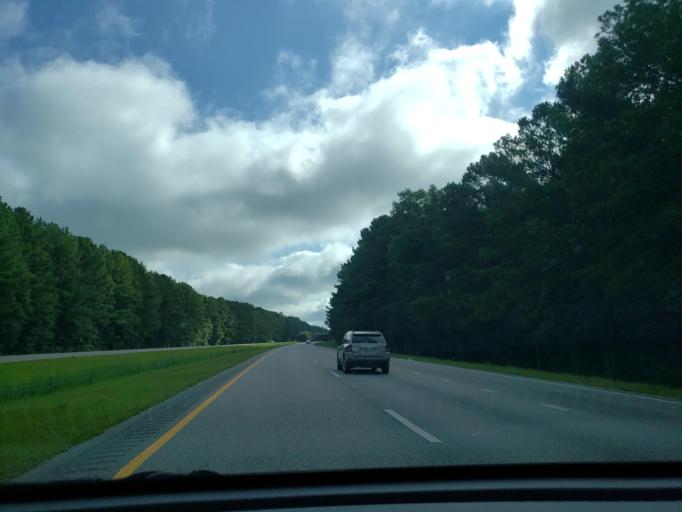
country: US
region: North Carolina
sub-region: Nash County
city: Spring Hope
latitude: 35.9429
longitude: -78.0476
